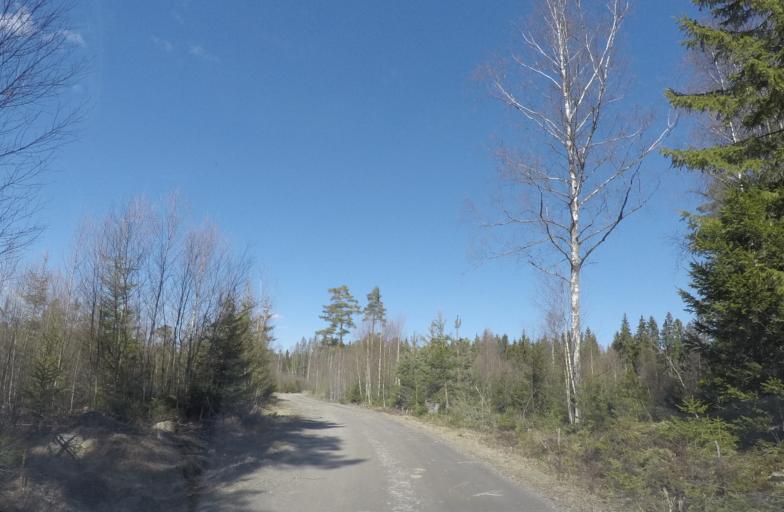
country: SE
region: Vaestmanland
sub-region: Vasteras
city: Vasteras
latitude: 59.6673
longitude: 16.4985
